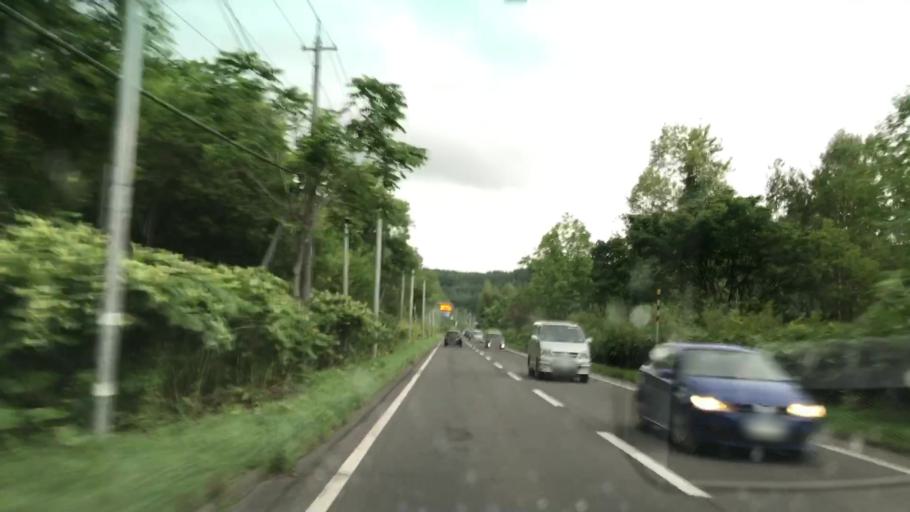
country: JP
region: Hokkaido
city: Niseko Town
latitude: 42.8254
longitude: 141.0047
